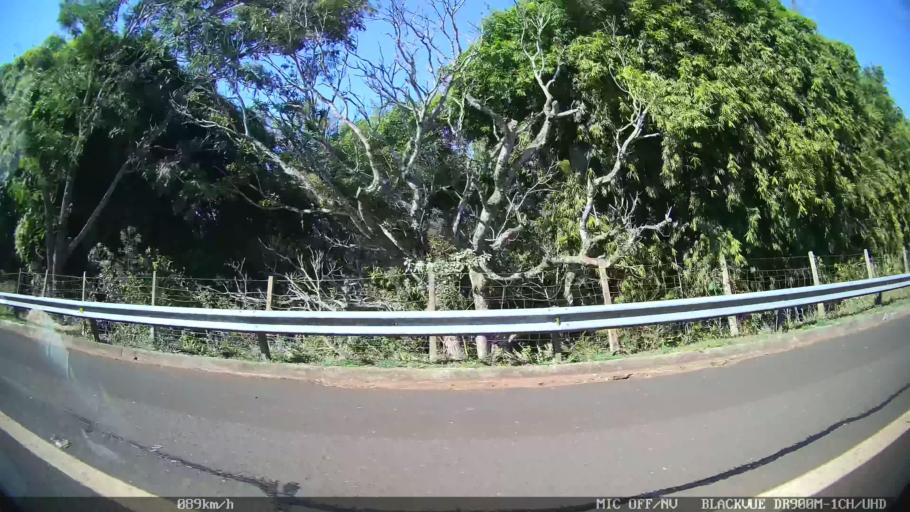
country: BR
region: Sao Paulo
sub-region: Batatais
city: Batatais
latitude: -20.7297
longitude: -47.5218
